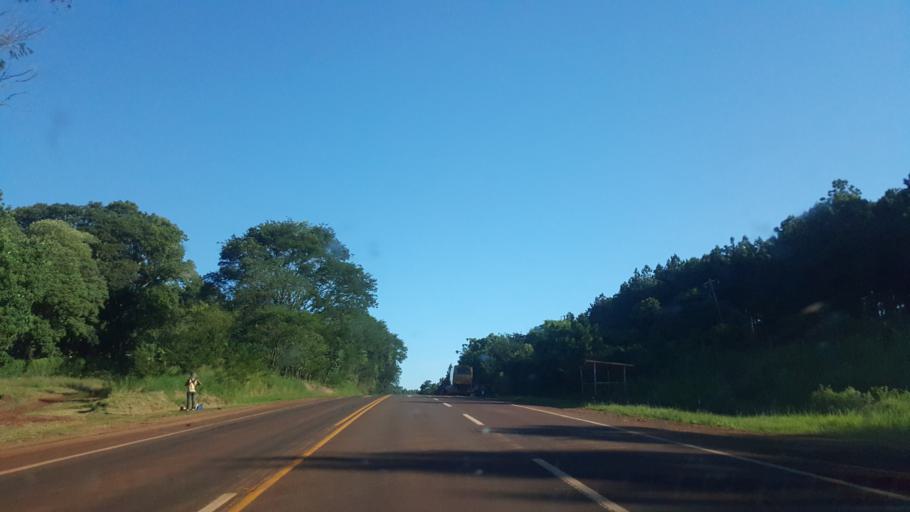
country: AR
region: Misiones
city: Puerto Esperanza
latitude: -26.1589
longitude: -54.5834
